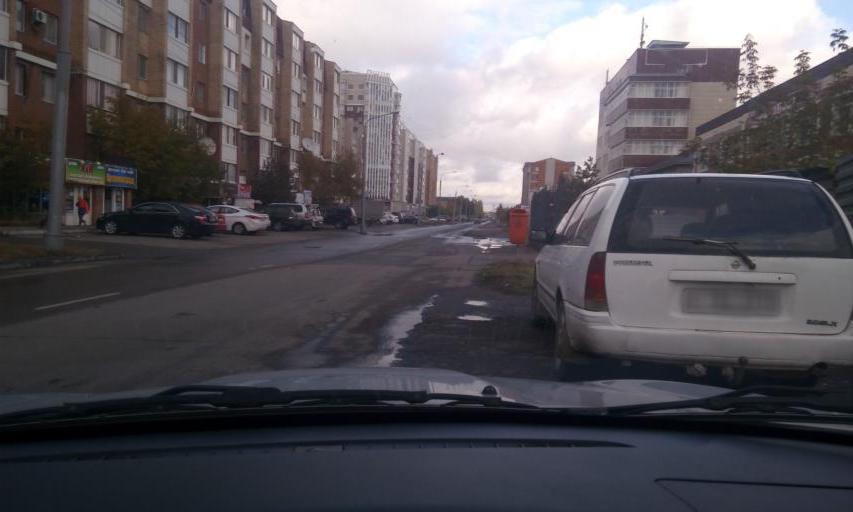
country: KZ
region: Astana Qalasy
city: Astana
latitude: 51.1672
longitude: 71.4643
